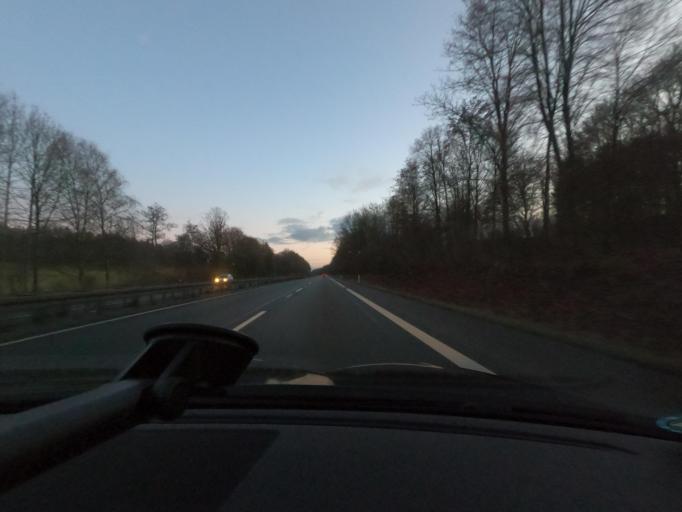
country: DE
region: Lower Saxony
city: Hoerden
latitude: 51.6996
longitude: 10.2845
